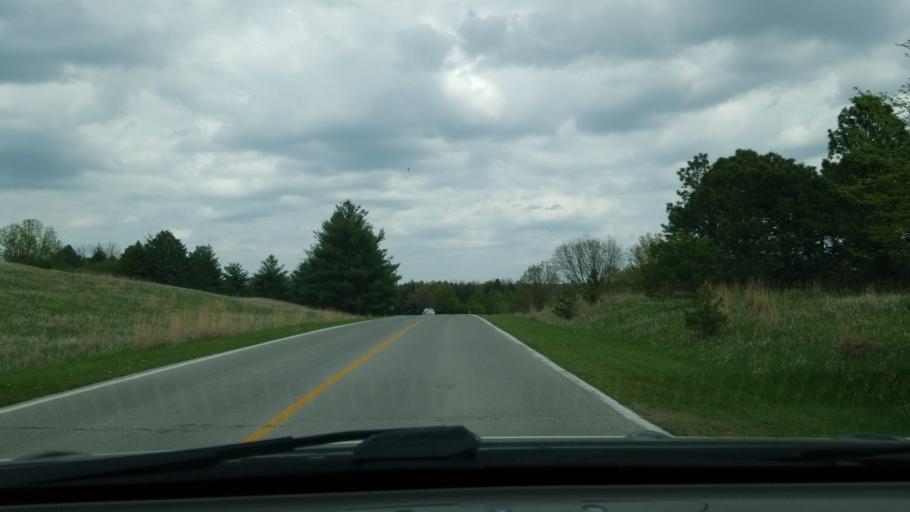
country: US
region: Nebraska
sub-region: Sarpy County
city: Chalco
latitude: 41.1642
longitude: -96.1582
